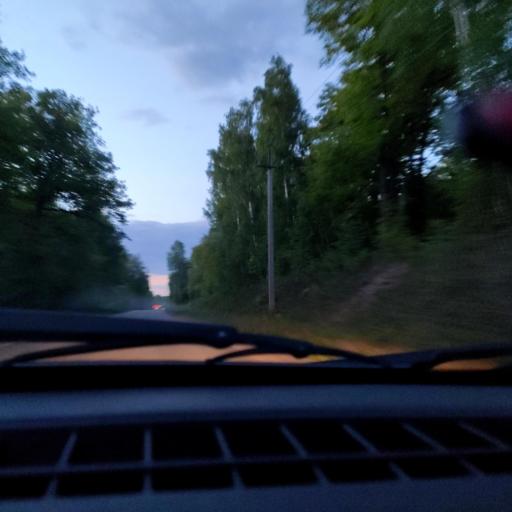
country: RU
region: Bashkortostan
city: Avdon
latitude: 54.6504
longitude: 55.5808
